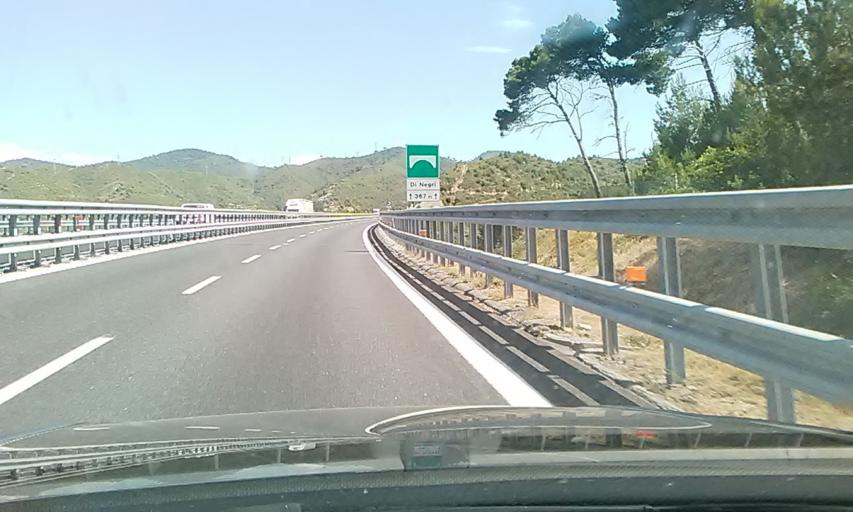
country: IT
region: Liguria
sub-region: Provincia di Savona
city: Laigueglia
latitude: 43.9847
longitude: 8.1364
